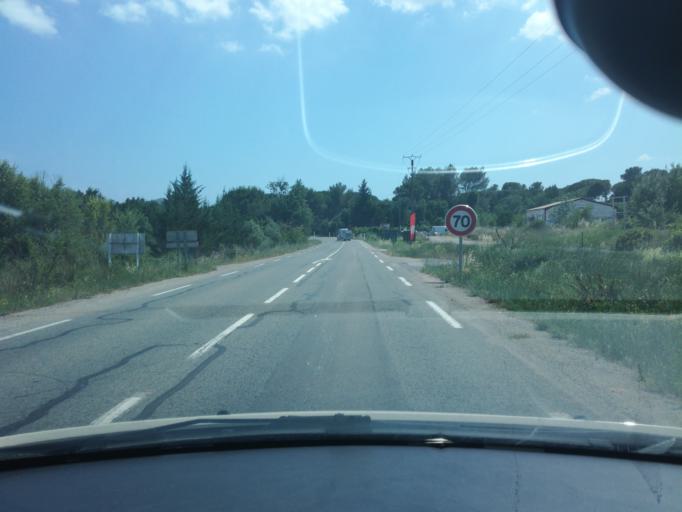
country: FR
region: Provence-Alpes-Cote d'Azur
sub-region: Departement du Var
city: Le Muy
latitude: 43.4900
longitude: 6.5651
